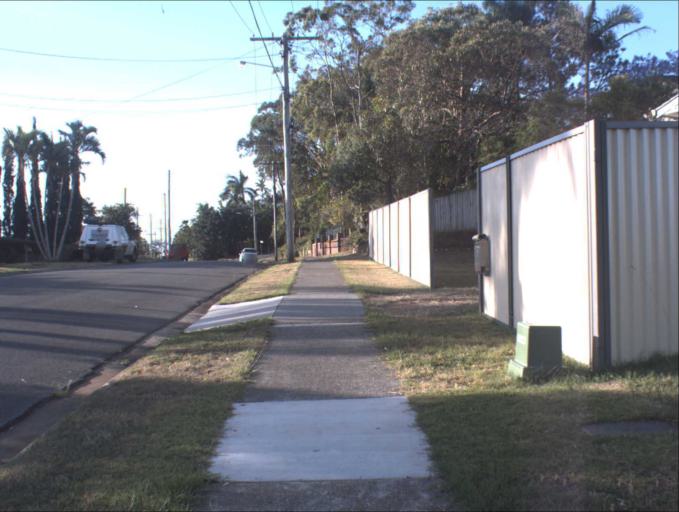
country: AU
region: Queensland
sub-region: Logan
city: Beenleigh
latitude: -27.6768
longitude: 153.2039
